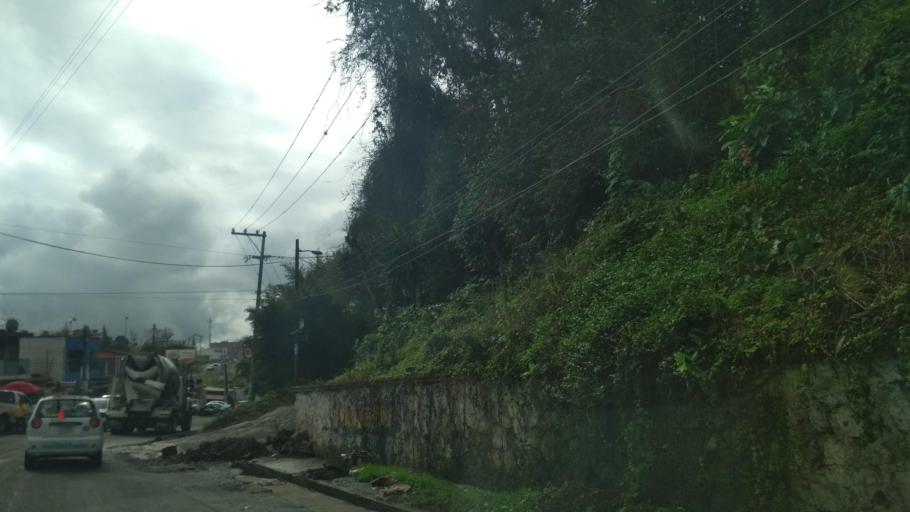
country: MX
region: Veracruz
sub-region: Emiliano Zapata
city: Las Trancas
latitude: 19.5052
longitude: -96.8625
